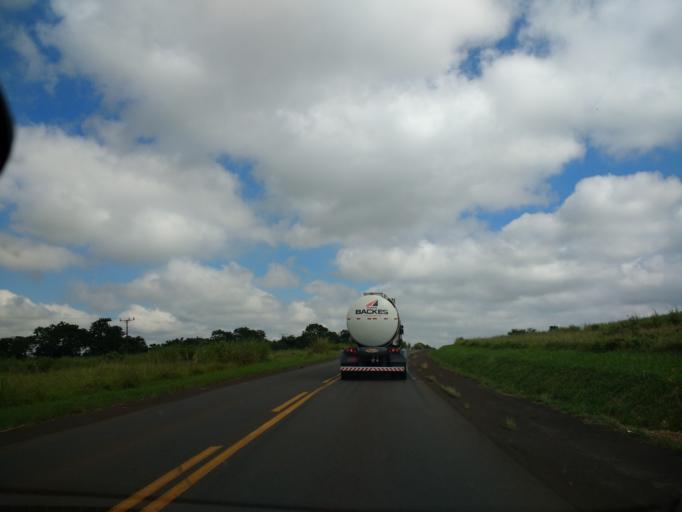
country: BR
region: Parana
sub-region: Cruzeiro Do Oeste
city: Cruzeiro do Oeste
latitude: -23.7715
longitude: -53.0145
